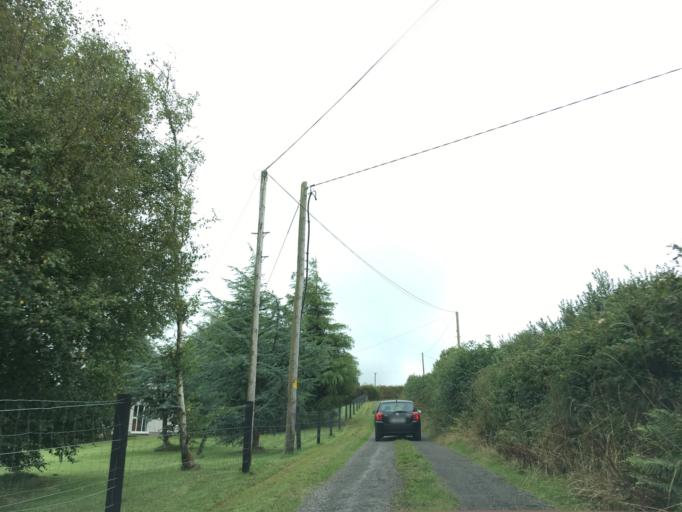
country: IE
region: Munster
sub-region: An Clar
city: Ennis
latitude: 52.7293
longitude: -9.0894
